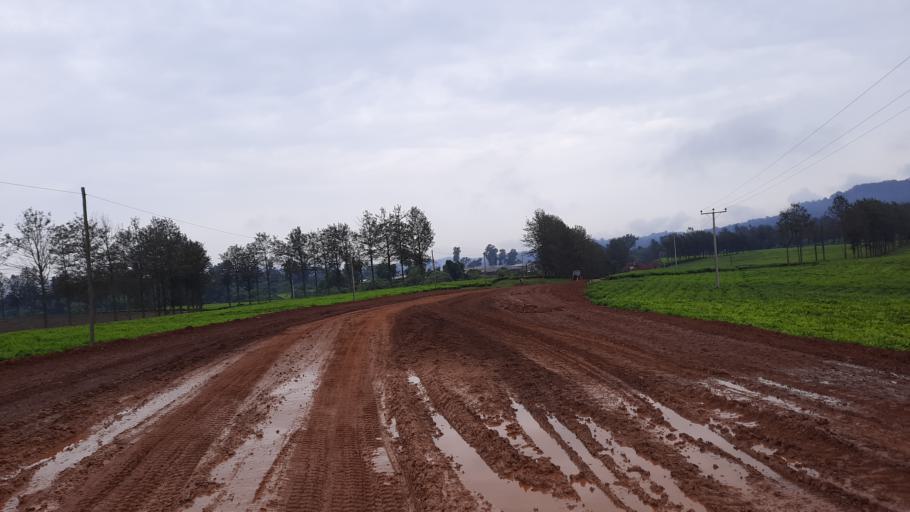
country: ET
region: Oromiya
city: Gore
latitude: 7.8561
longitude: 35.4754
